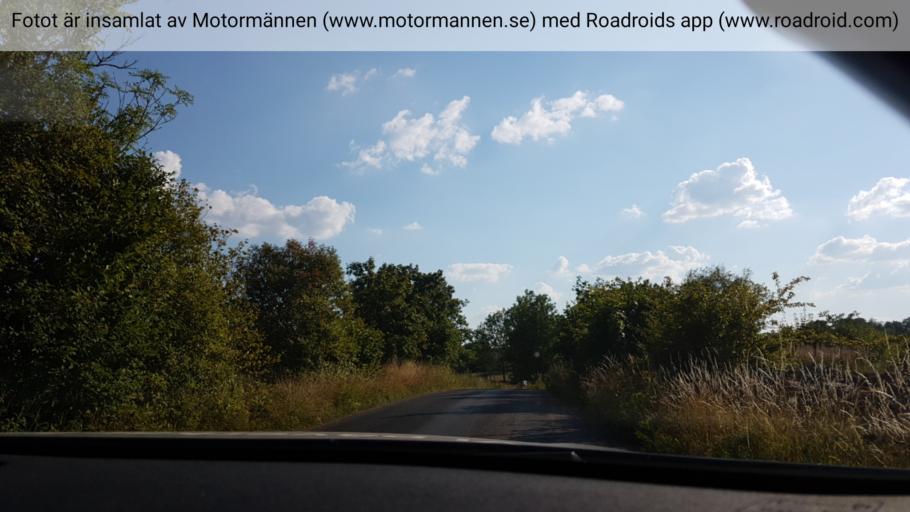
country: SE
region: Vaestra Goetaland
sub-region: Skovde Kommun
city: Stopen
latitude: 58.5040
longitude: 13.8049
